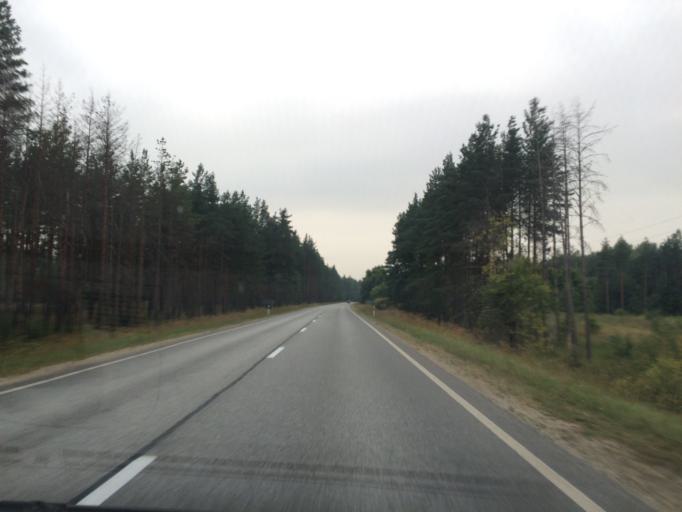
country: LV
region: Varaklani
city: Varaklani
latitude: 56.5488
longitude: 26.5892
